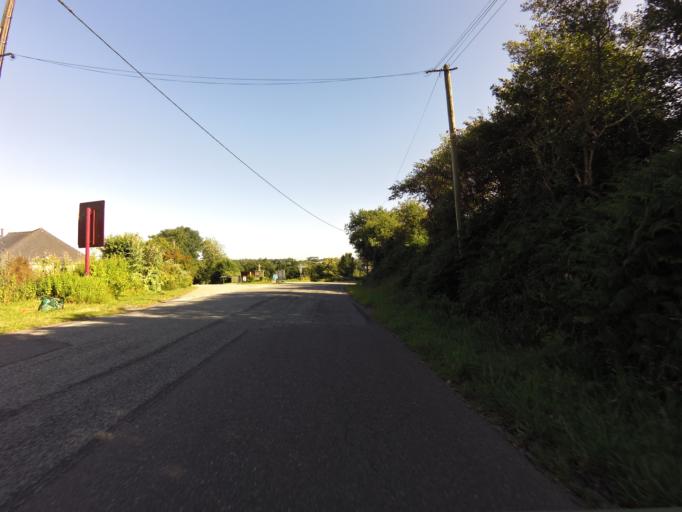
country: FR
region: Brittany
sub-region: Departement du Morbihan
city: Limerzel
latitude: 47.6317
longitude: -2.3541
